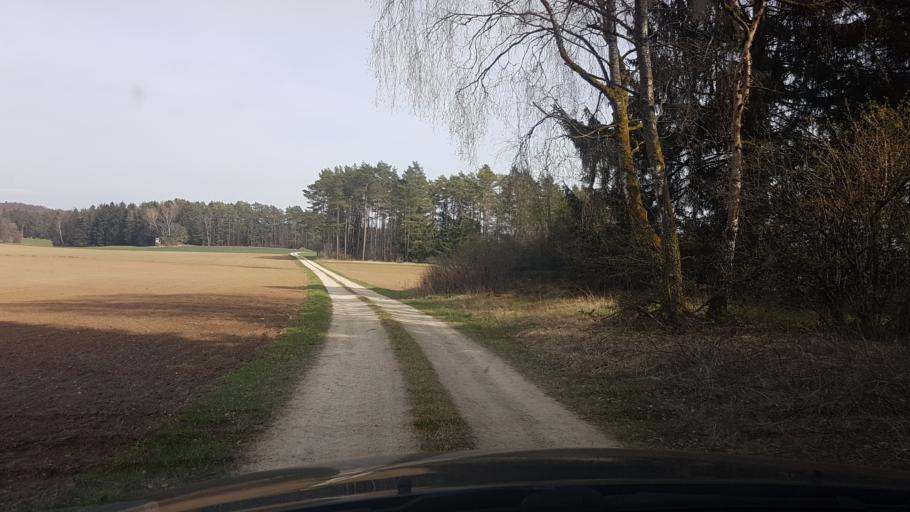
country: DE
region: Bavaria
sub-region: Upper Franconia
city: Wattendorf
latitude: 49.9950
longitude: 11.1195
